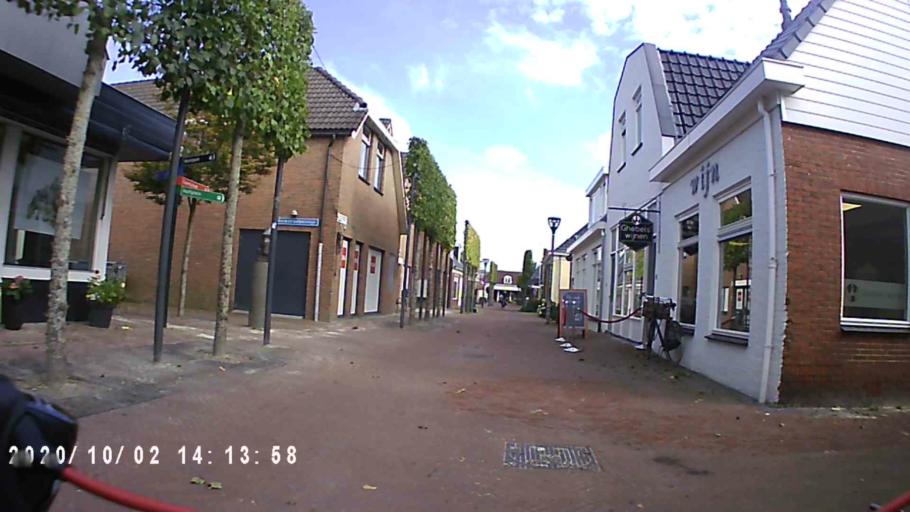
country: NL
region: Groningen
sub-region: Gemeente Zuidhorn
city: Zuidhorn
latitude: 53.2437
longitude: 6.4061
